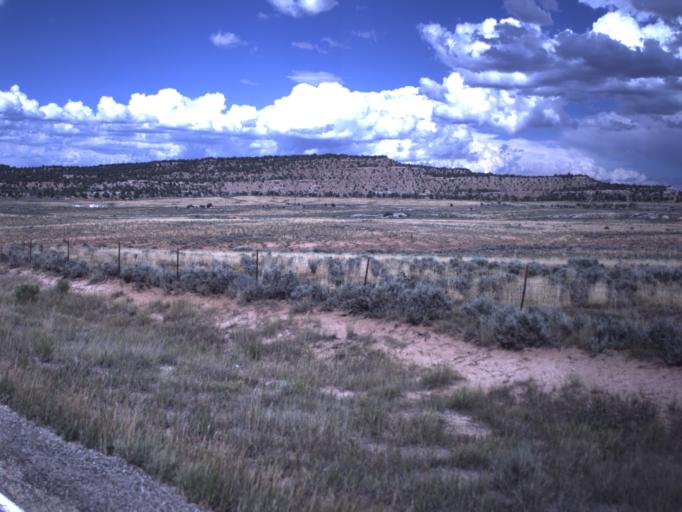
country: US
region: Utah
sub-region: Duchesne County
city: Duchesne
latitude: 40.2139
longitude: -110.7279
